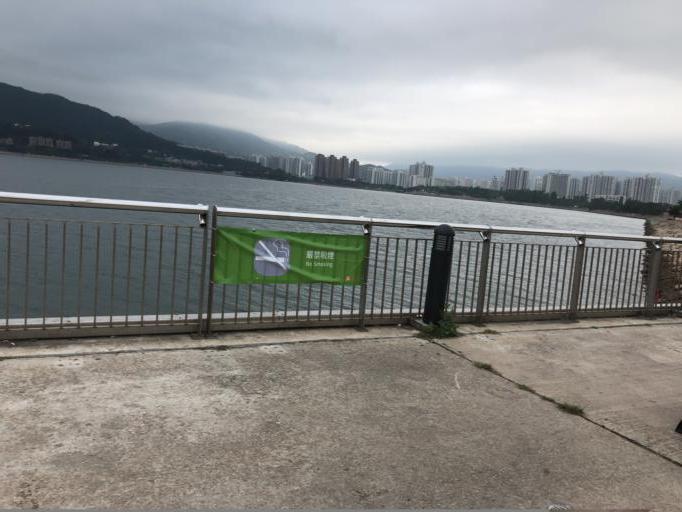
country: HK
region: Tai Po
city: Tai Po
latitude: 22.4509
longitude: 114.1929
